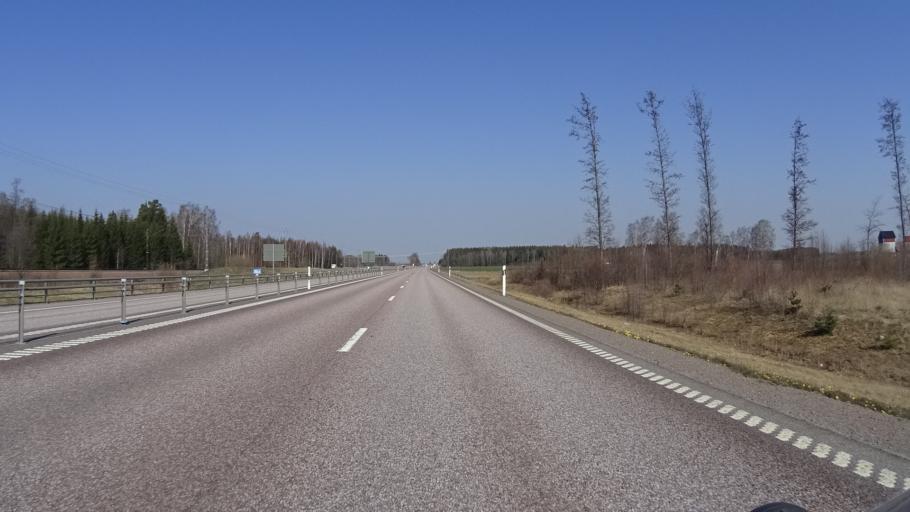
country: SE
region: OEstergoetland
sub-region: Motala Kommun
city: Stenstorp
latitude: 58.4177
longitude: 15.0737
